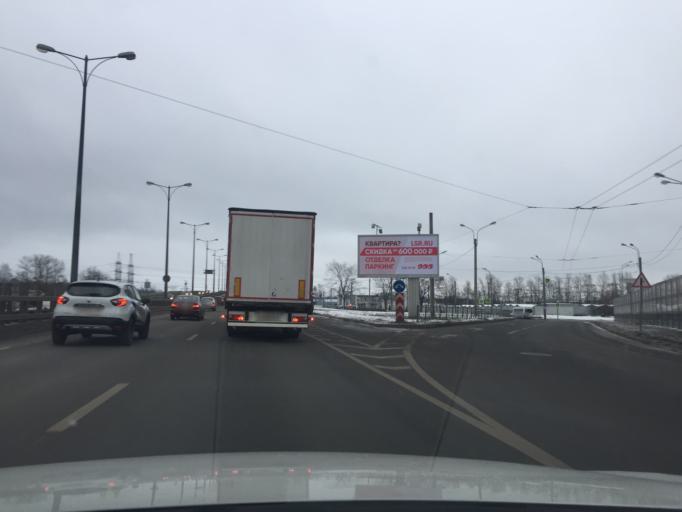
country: RU
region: St.-Petersburg
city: Krasnogvargeisky
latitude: 59.9453
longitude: 30.5006
